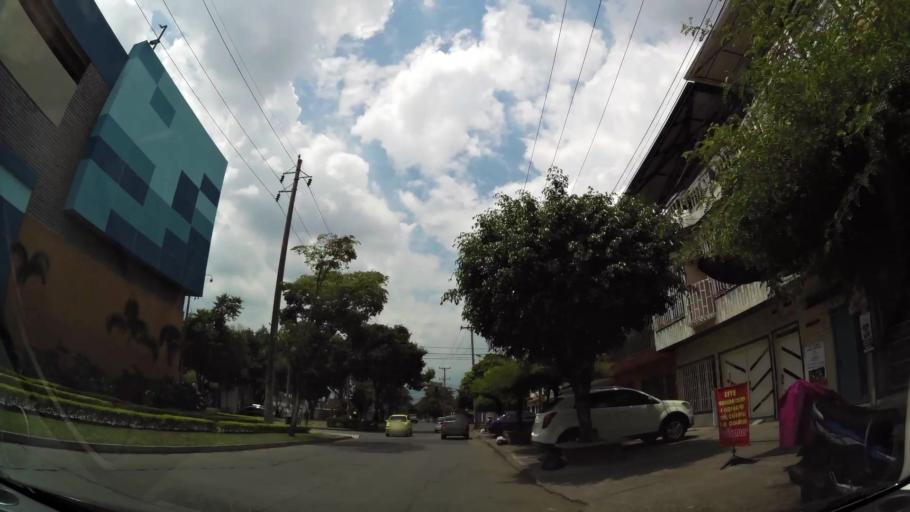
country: CO
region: Valle del Cauca
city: Cali
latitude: 3.4650
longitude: -76.5026
